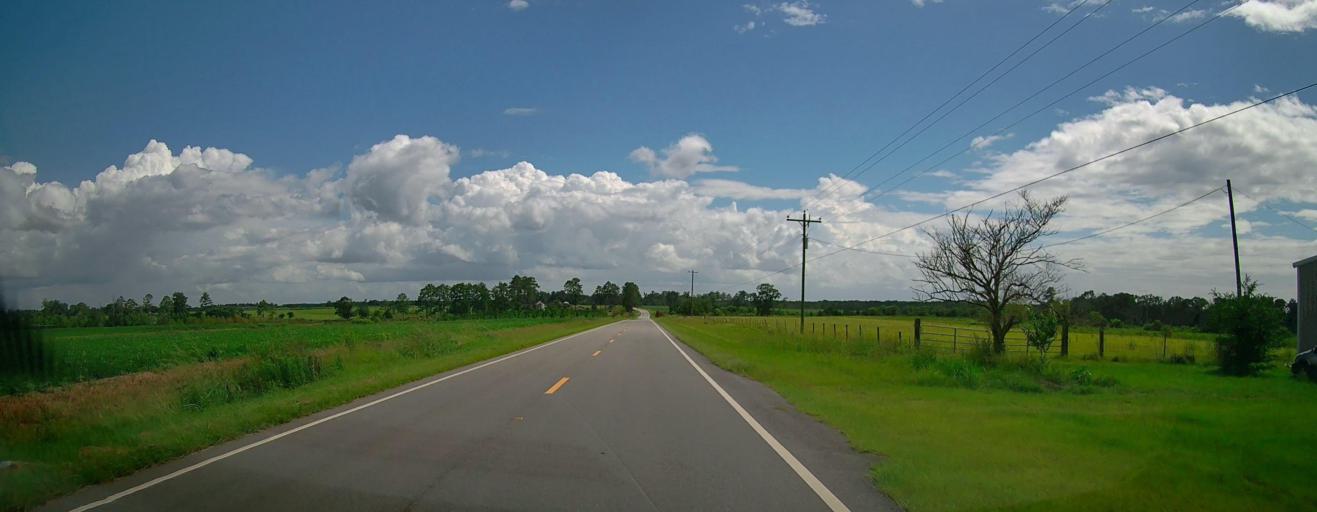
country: US
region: Georgia
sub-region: Irwin County
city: Ocilla
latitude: 31.6122
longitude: -83.1657
